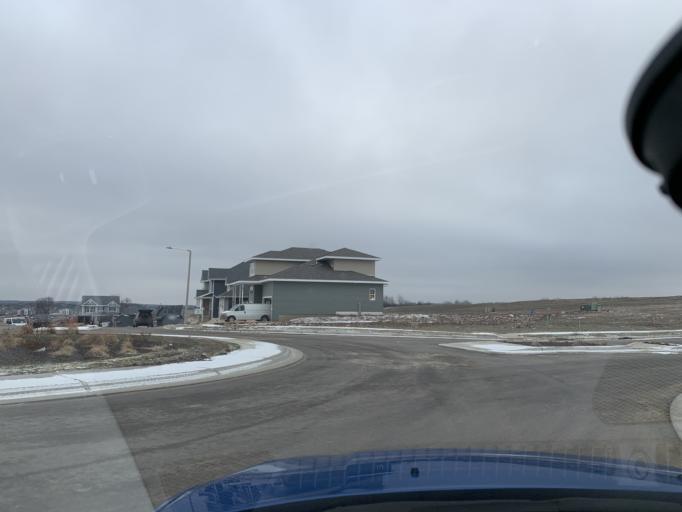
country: US
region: Wisconsin
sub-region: Dane County
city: Middleton
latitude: 43.0703
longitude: -89.5668
